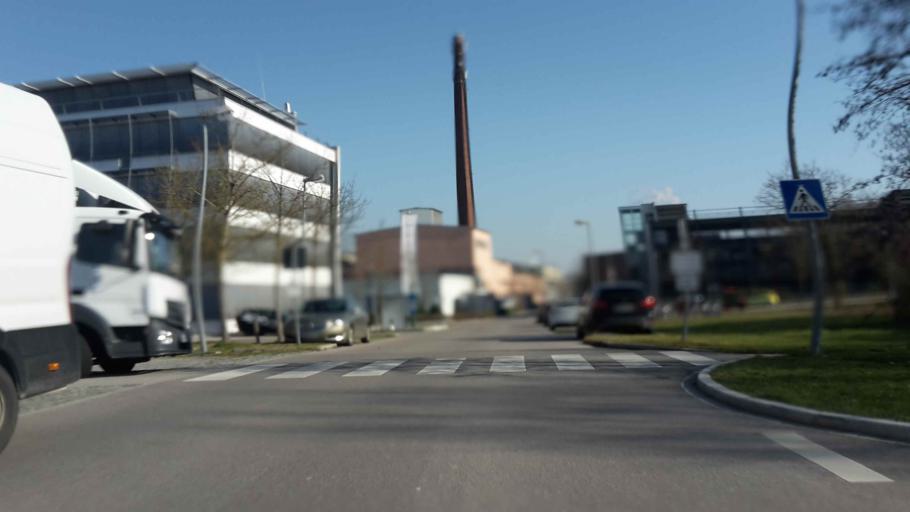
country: DE
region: Bavaria
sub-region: Upper Bavaria
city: Unterfoehring
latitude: 48.2078
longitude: 11.6583
